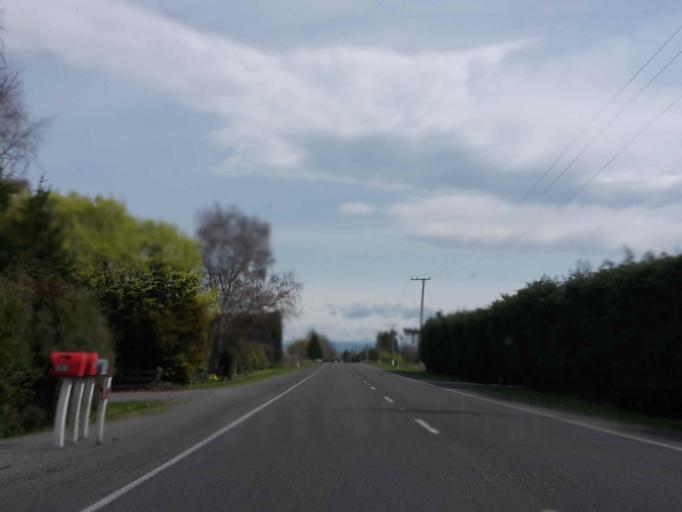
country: NZ
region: Canterbury
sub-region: Waimakariri District
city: Kaiapoi
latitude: -43.4012
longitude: 172.6118
